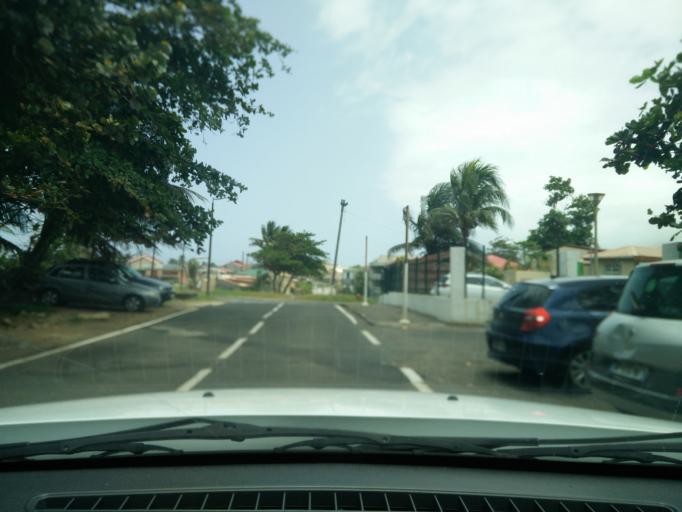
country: GP
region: Guadeloupe
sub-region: Guadeloupe
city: Capesterre-Belle-Eau
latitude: 16.0481
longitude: -61.5606
